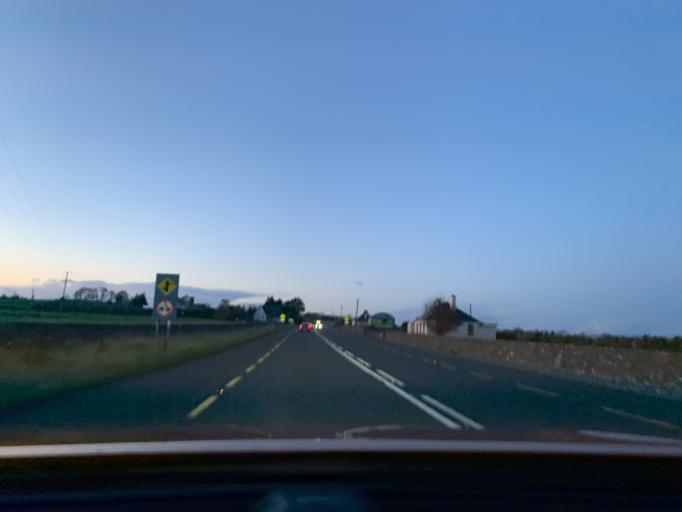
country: IE
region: Connaught
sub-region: Roscommon
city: Boyle
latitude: 53.9643
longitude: -8.1959
